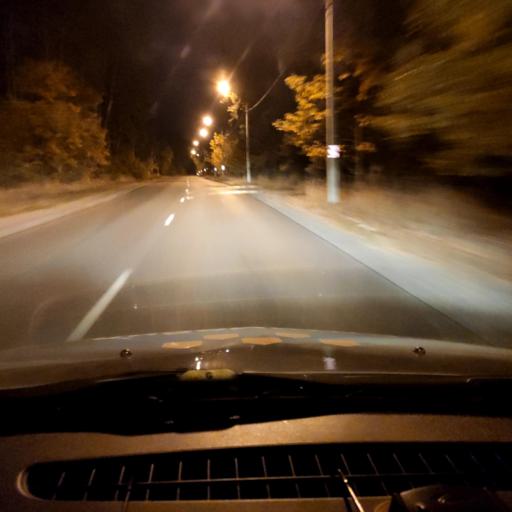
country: RU
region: Voronezj
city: Somovo
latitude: 51.7143
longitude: 39.3255
